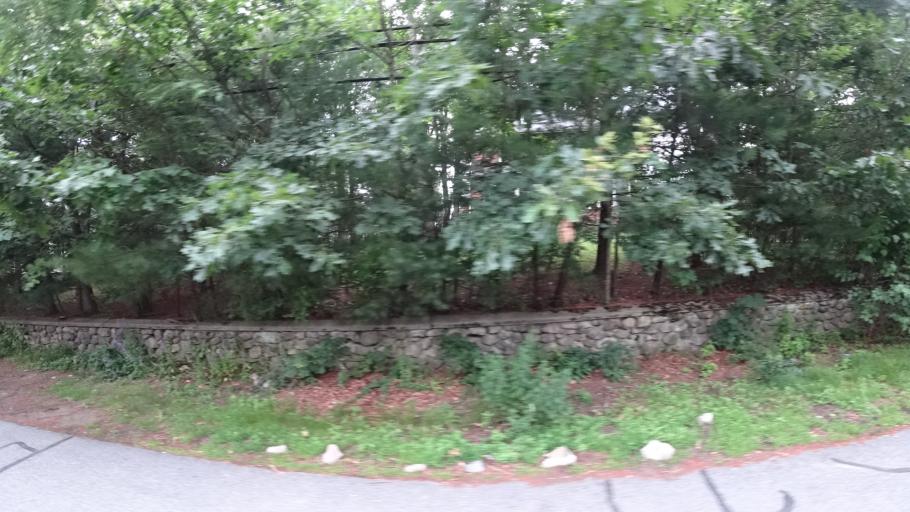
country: US
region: Massachusetts
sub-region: Norfolk County
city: Dedham
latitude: 42.2371
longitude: -71.1534
